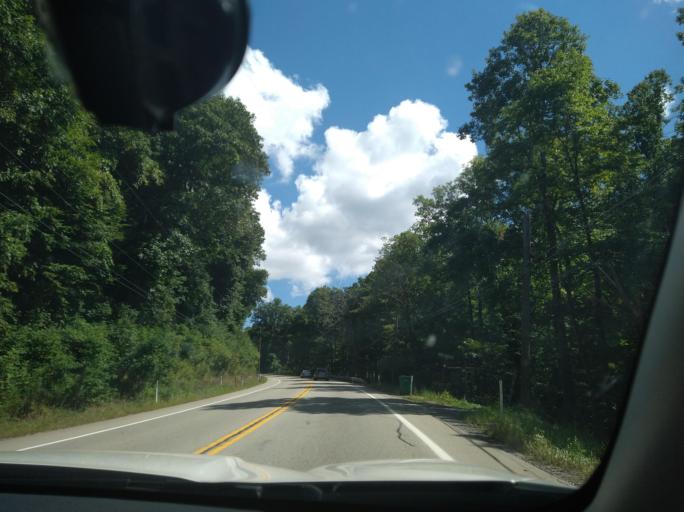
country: US
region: Pennsylvania
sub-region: Fayette County
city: Bear Rocks
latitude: 40.0750
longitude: -79.3120
